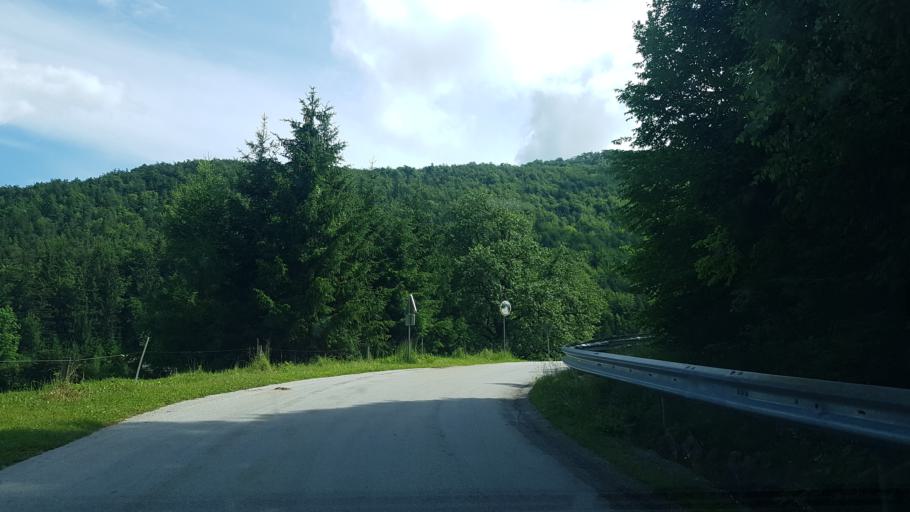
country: SI
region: Velenje
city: Velenje
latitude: 46.3863
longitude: 15.1697
